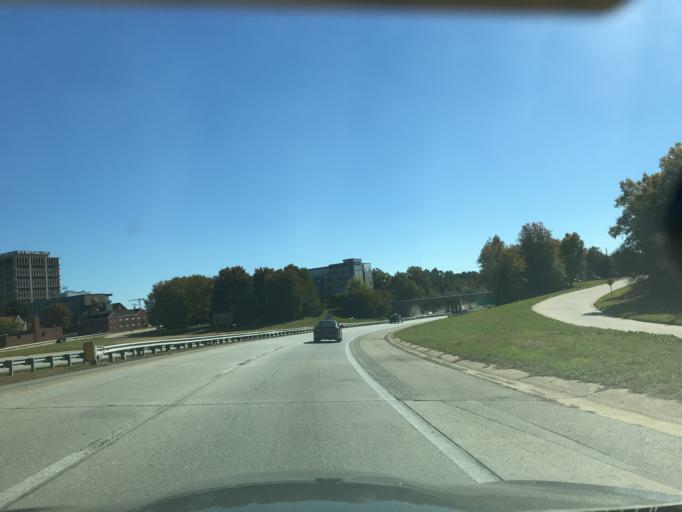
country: US
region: North Carolina
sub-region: Durham County
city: Durham
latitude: 35.9990
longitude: -78.9131
